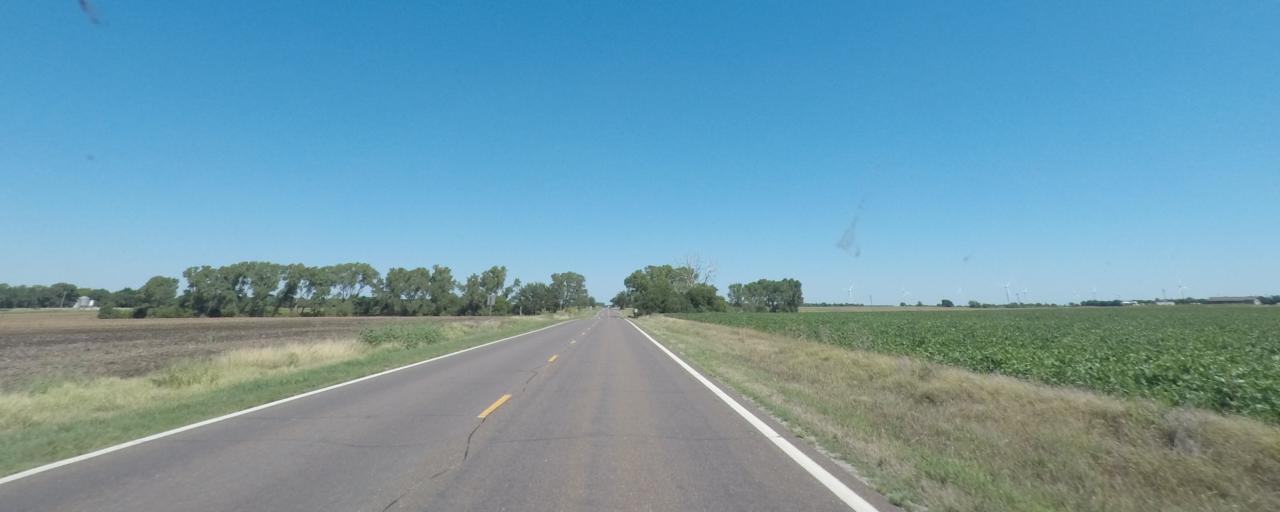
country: US
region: Kansas
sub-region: Sumner County
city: Wellington
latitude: 37.1119
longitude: -97.4016
